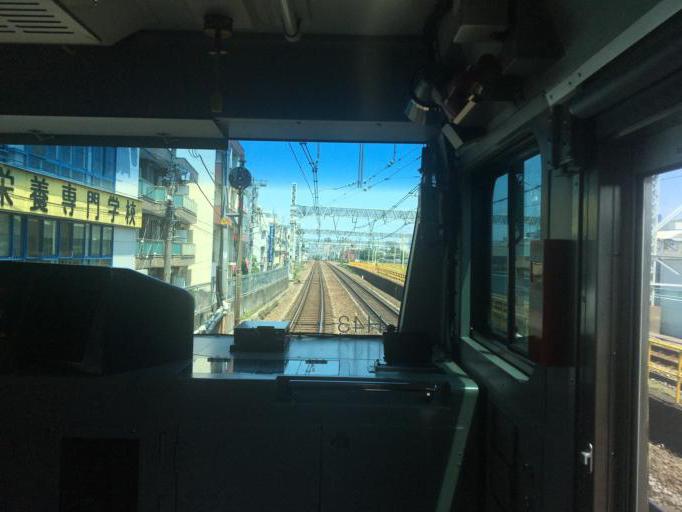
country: JP
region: Tokyo
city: Tokyo
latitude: 35.7061
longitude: 139.6689
